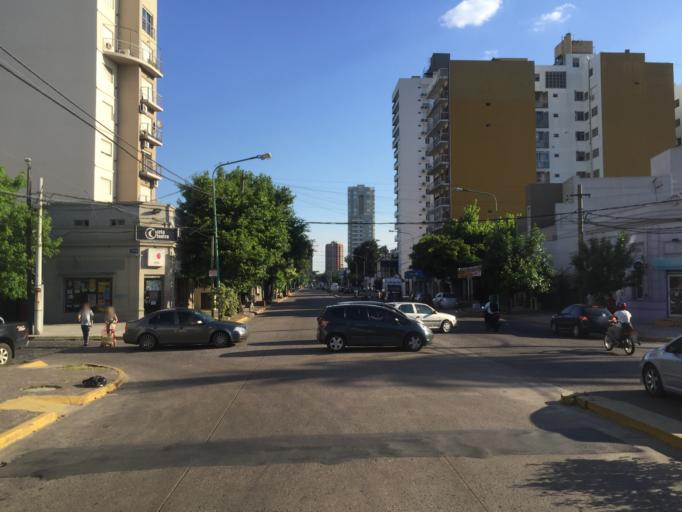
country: AR
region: Buenos Aires
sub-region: Partido de Lomas de Zamora
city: Lomas de Zamora
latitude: -34.7646
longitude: -58.3966
